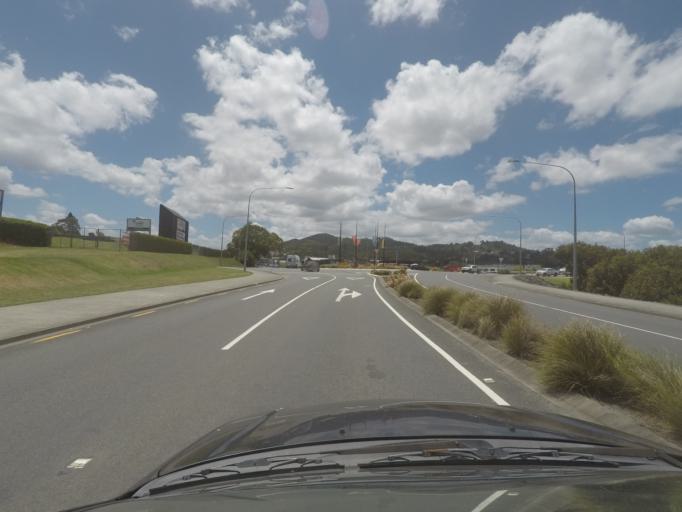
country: NZ
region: Northland
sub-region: Whangarei
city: Whangarei
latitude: -35.7356
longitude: 174.3326
